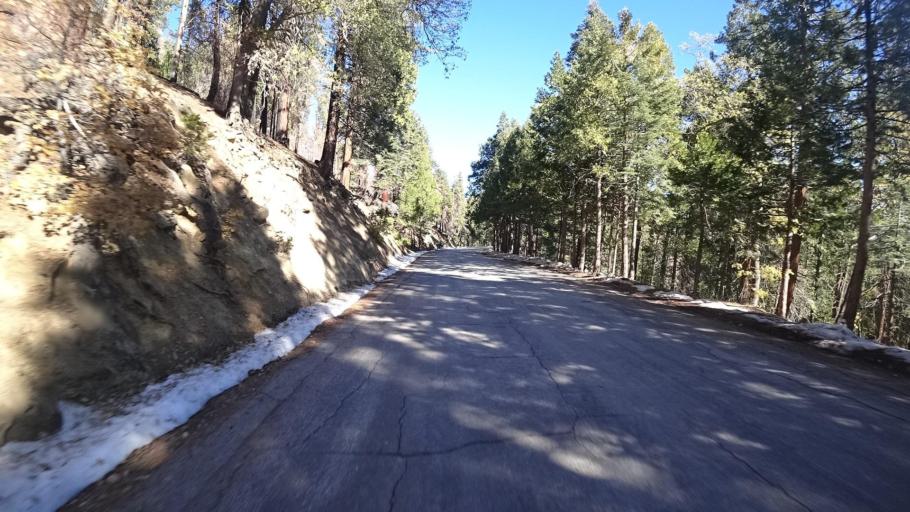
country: US
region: California
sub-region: Kern County
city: Alta Sierra
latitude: 35.7341
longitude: -118.5588
